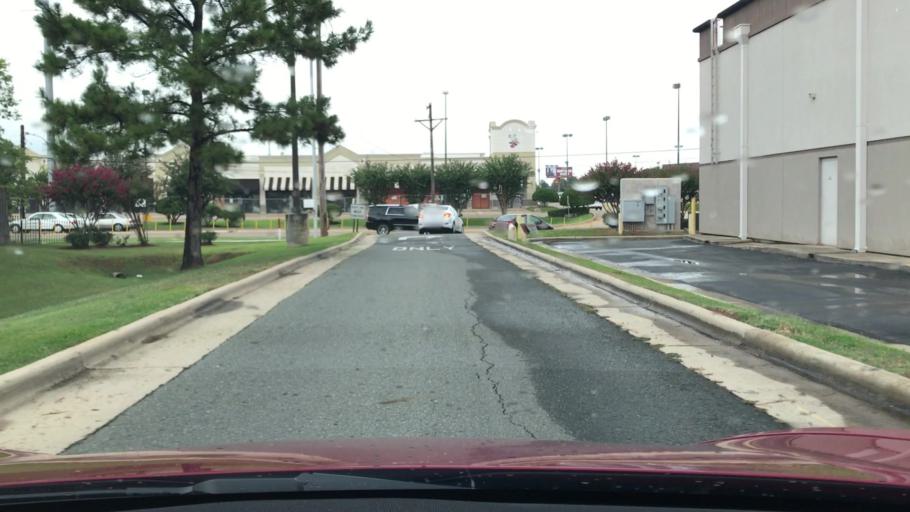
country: US
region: Louisiana
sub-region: Bossier Parish
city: Bossier City
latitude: 32.4429
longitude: -93.7218
